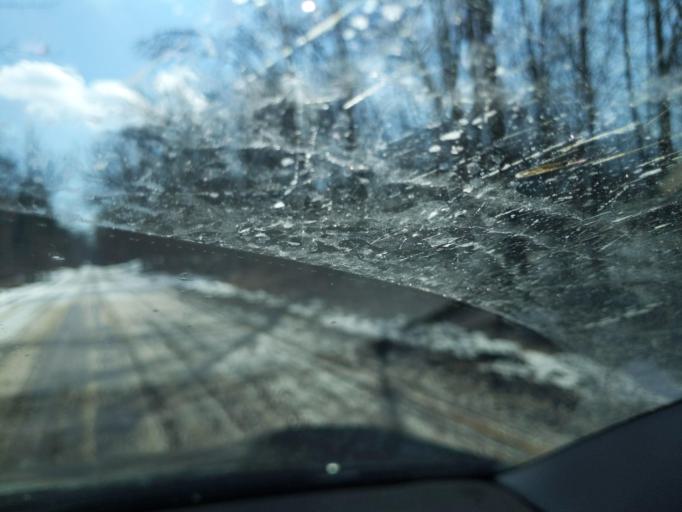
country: US
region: Michigan
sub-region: Livingston County
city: Fowlerville
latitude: 42.5458
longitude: -84.0883
